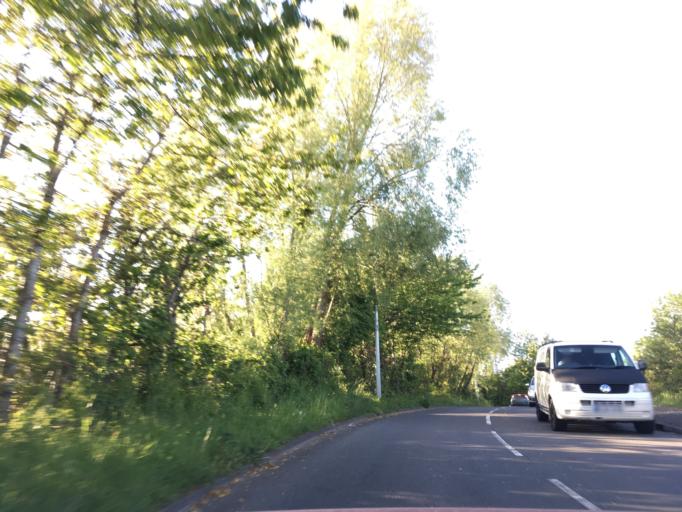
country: GB
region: Wales
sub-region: Newport
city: Marshfield
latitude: 51.5291
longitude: -3.0947
